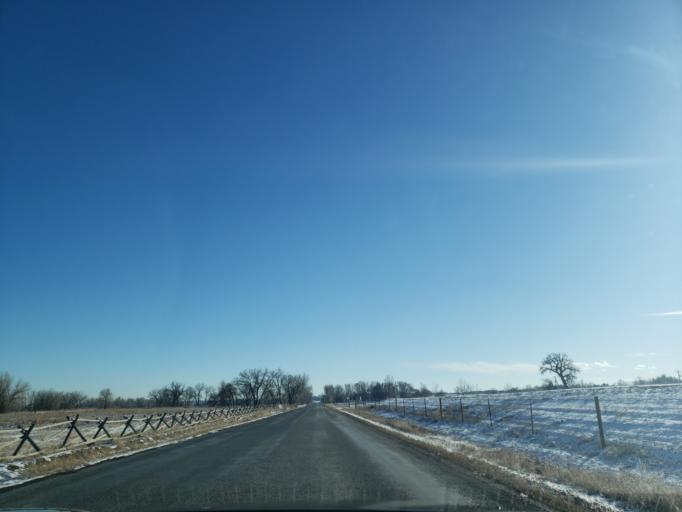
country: US
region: Colorado
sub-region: Larimer County
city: Fort Collins
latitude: 40.5341
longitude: -105.0013
